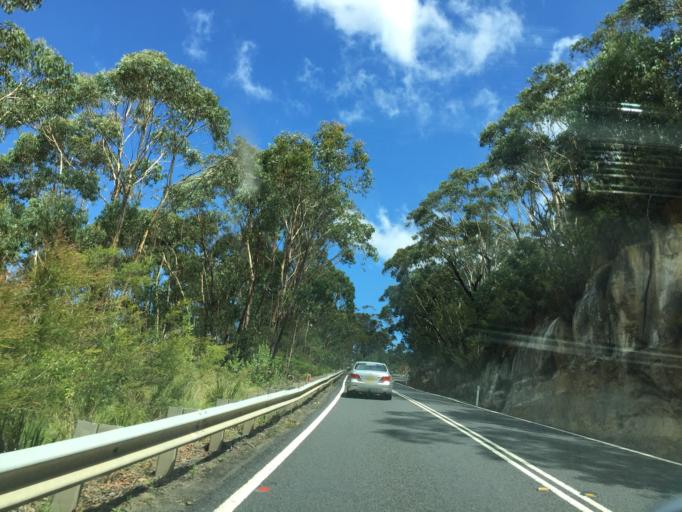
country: AU
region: New South Wales
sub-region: Blue Mountains Municipality
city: Blackheath
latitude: -33.5522
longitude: 150.3803
